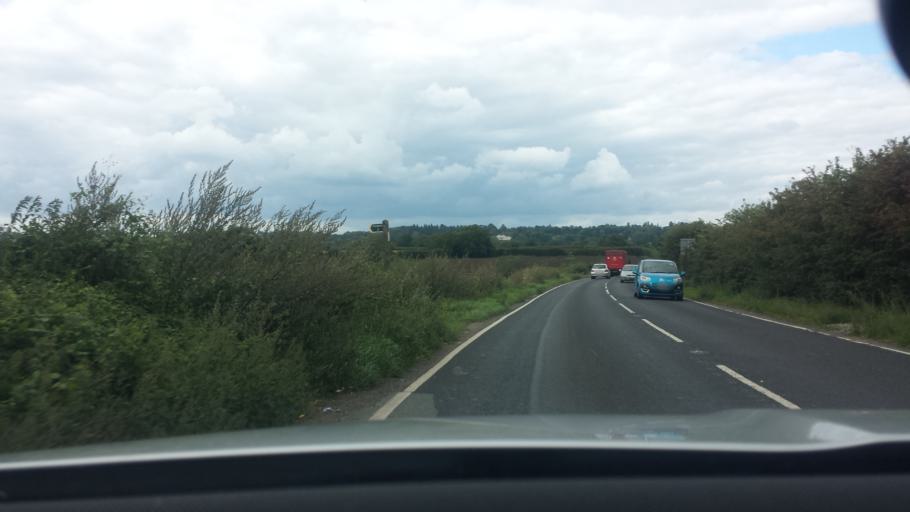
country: GB
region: England
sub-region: Kent
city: Marden
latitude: 51.2026
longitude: 0.5167
